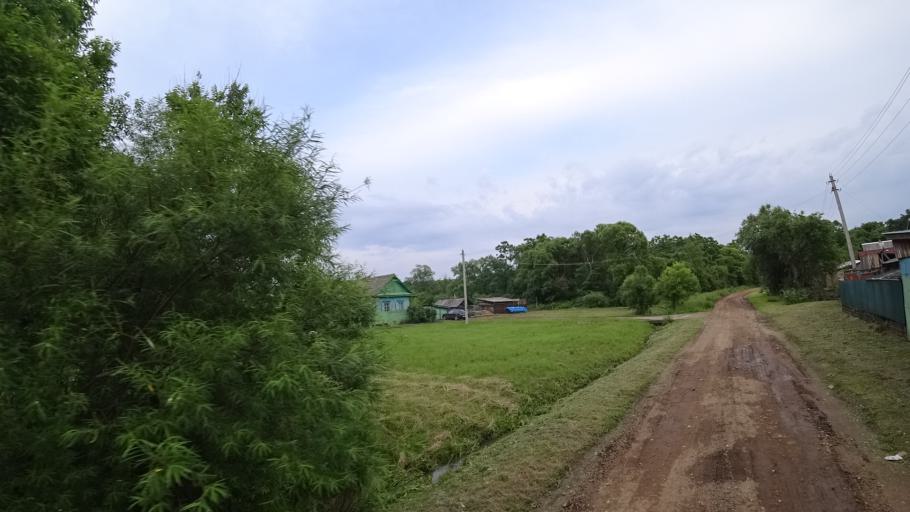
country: RU
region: Primorskiy
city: Novosysoyevka
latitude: 44.2399
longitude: 133.3778
